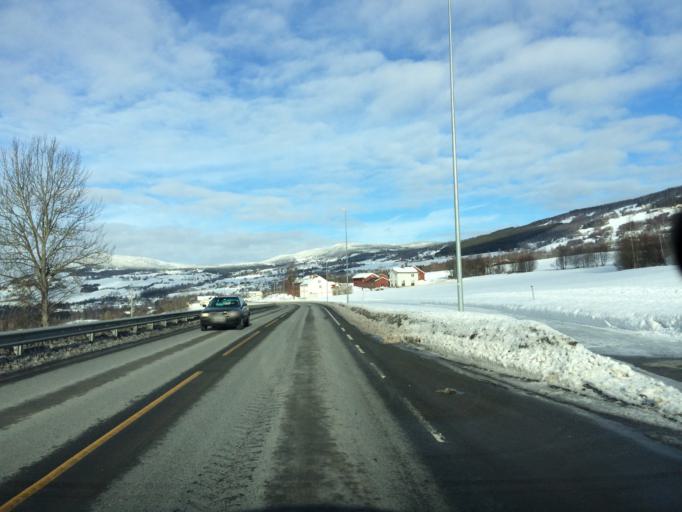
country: NO
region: Oppland
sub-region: Gausdal
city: Segalstad bru
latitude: 61.1971
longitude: 10.3093
